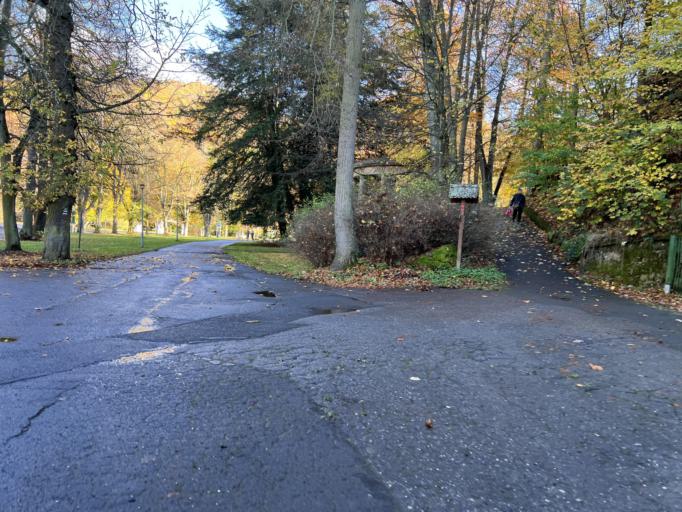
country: CZ
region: Karlovarsky
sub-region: Okres Karlovy Vary
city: Karlovy Vary
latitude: 50.2171
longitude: 12.8876
